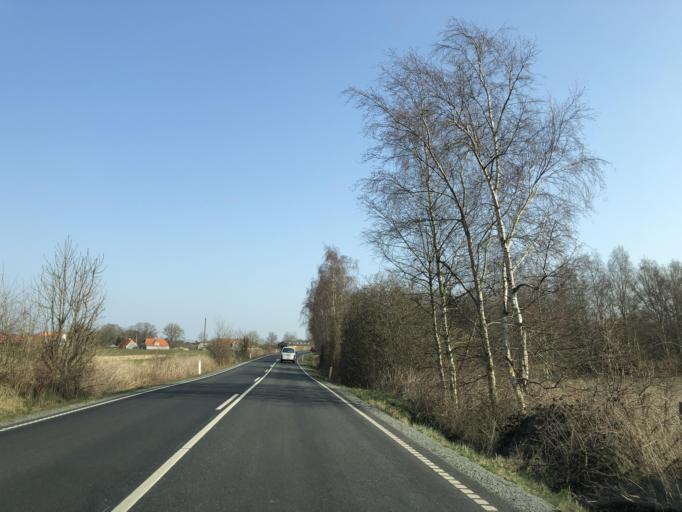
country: DK
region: South Denmark
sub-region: Sonderborg Kommune
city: Nordborg
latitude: 55.0257
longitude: 9.7840
